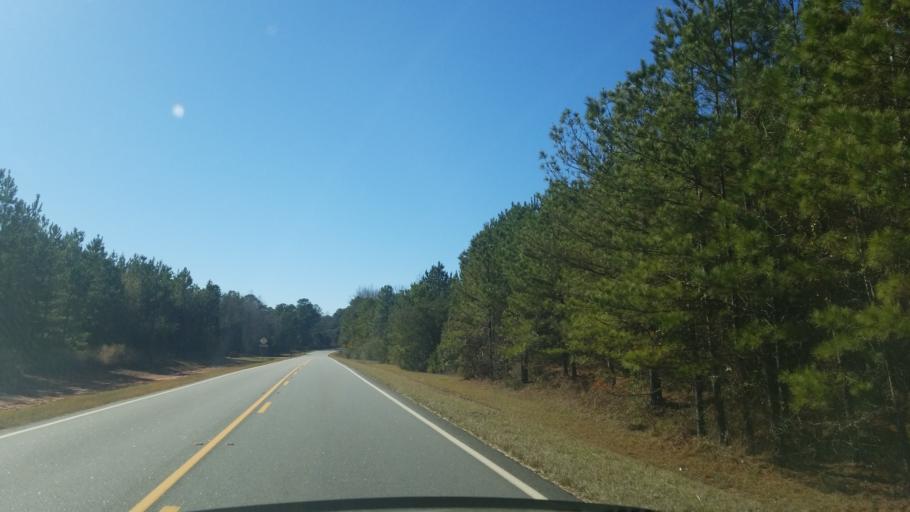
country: US
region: Georgia
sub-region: Talbot County
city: Sardis
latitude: 32.6349
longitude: -84.7229
